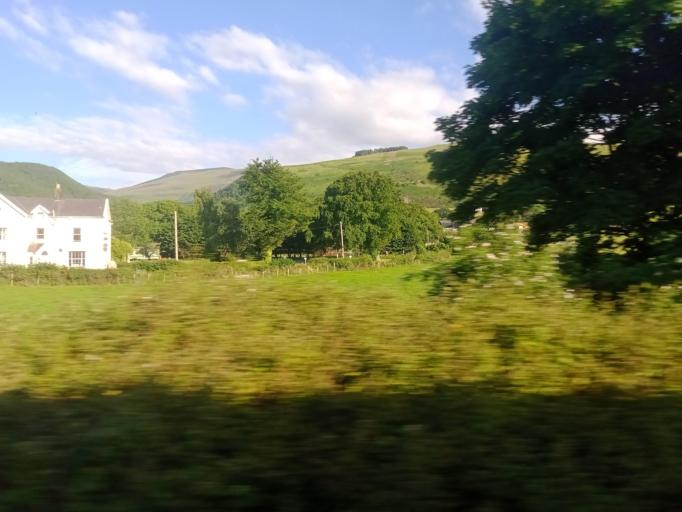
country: GB
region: Wales
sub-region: Gwynedd
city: Aber
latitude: 53.2381
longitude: -4.0241
